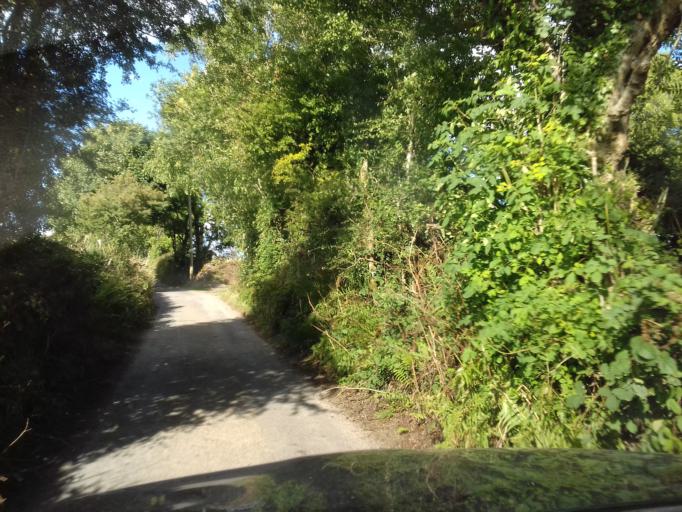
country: IE
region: Leinster
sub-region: Kilkenny
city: Graiguenamanagh
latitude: 52.5485
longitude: -7.0256
